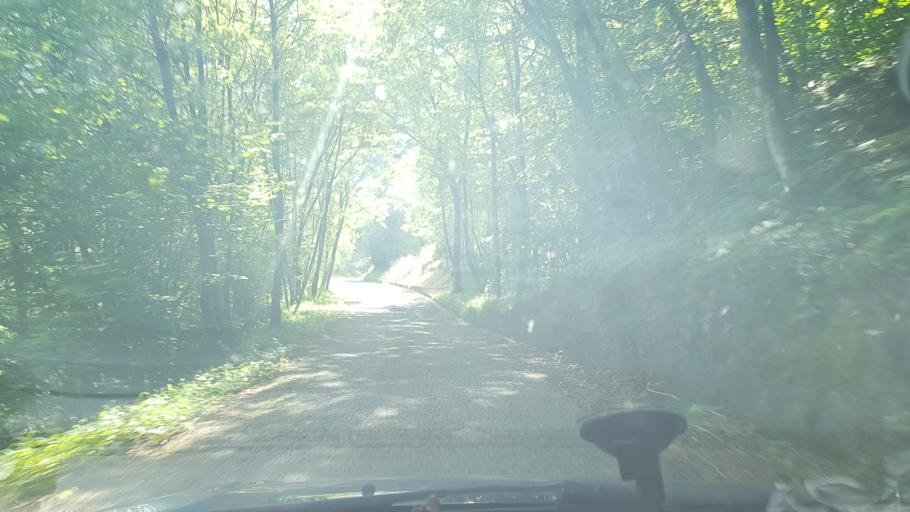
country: IT
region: Friuli Venezia Giulia
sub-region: Provincia di Udine
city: Prato
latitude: 46.3527
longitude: 13.3813
